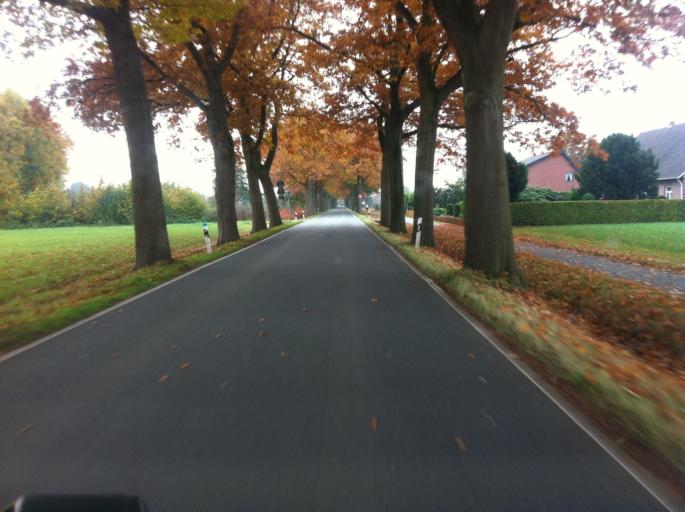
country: DE
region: North Rhine-Westphalia
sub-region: Regierungsbezirk Munster
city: Vreden
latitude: 52.0157
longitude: 6.7972
